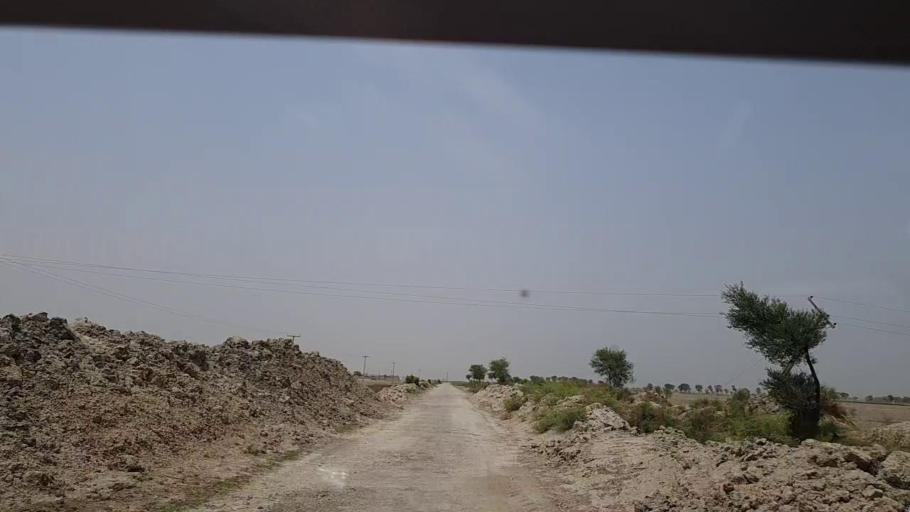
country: PK
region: Sindh
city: Khairpur Nathan Shah
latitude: 27.0356
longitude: 67.6192
